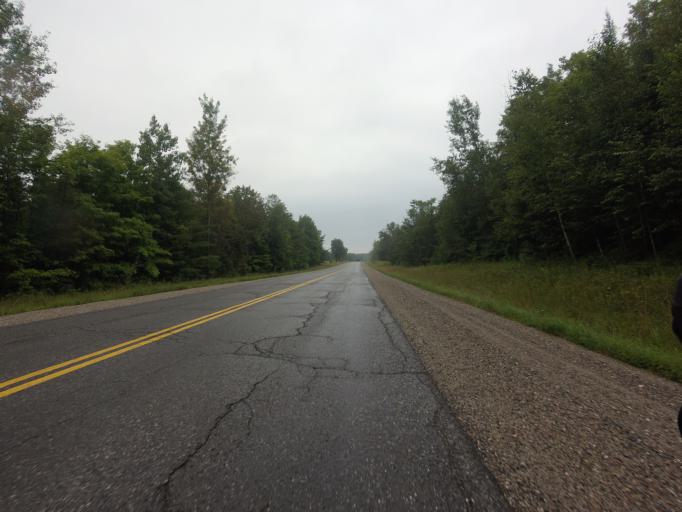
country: CA
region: Ontario
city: Carleton Place
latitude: 45.1360
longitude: -76.3290
